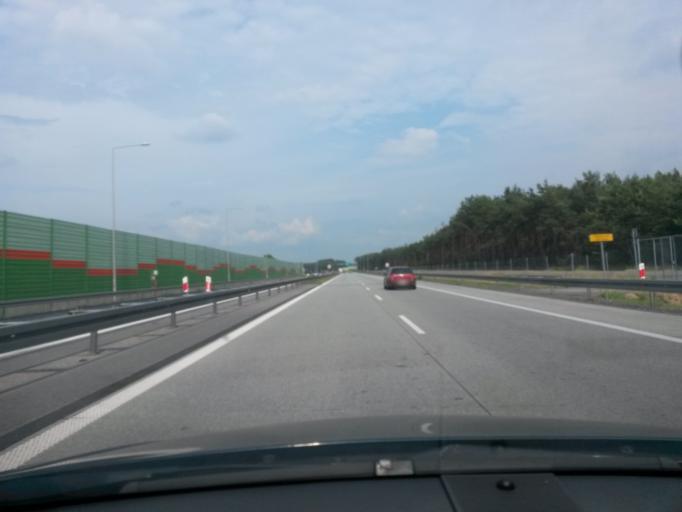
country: PL
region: Lodz Voivodeship
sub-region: Powiat tomaszowski
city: Ujazd
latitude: 51.5224
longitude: 19.9280
